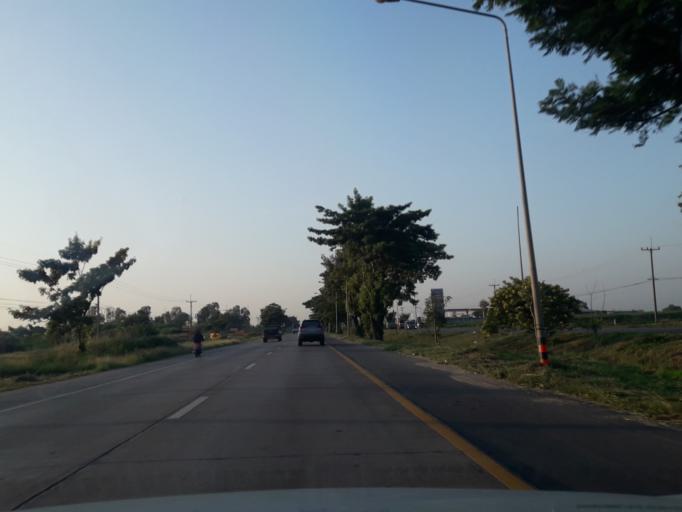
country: TH
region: Phra Nakhon Si Ayutthaya
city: Phra Nakhon Si Ayutthaya
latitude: 14.3342
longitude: 100.5280
